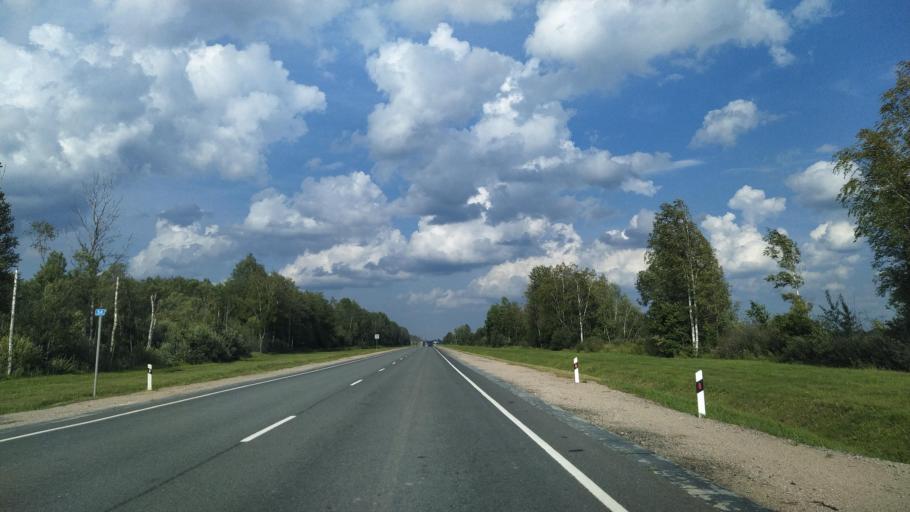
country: RU
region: Novgorod
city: Shimsk
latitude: 58.2285
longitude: 30.6409
